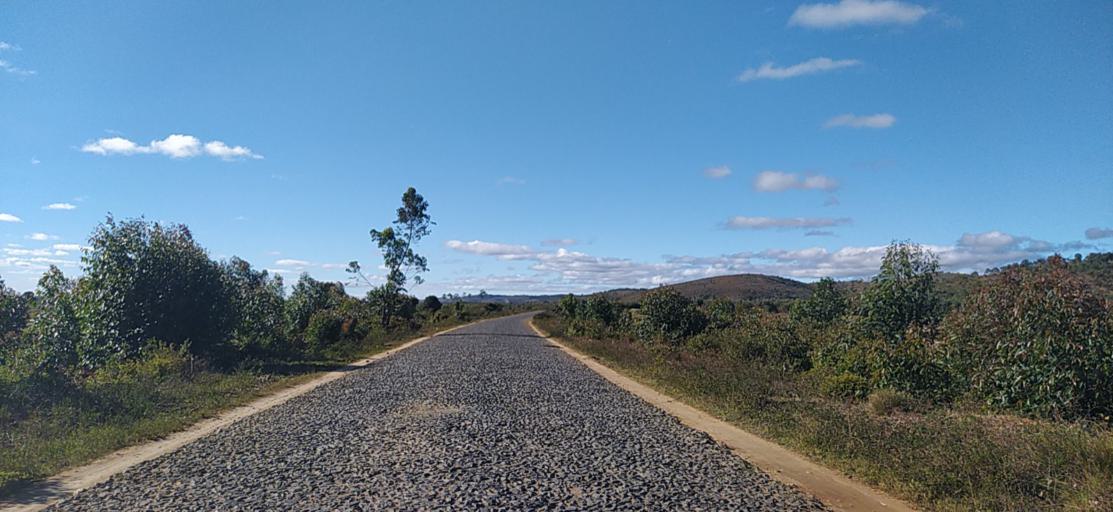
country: MG
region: Alaotra Mangoro
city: Moramanga
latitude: -18.7668
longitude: 48.2537
